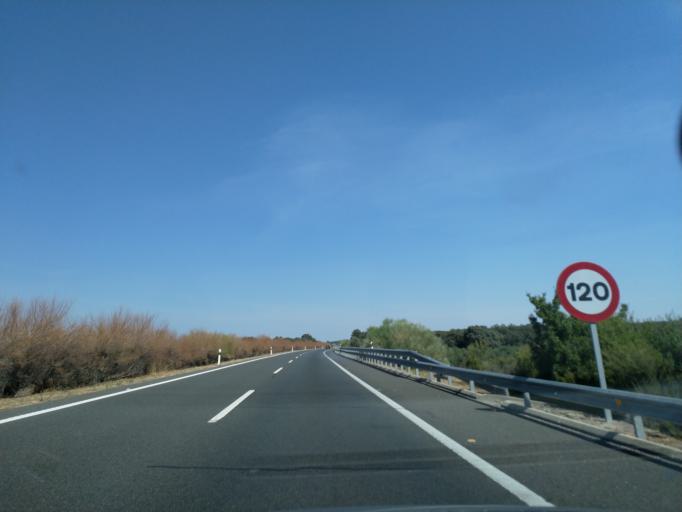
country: ES
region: Extremadura
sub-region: Provincia de Caceres
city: Aldea del Cano
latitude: 39.2967
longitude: -6.3307
